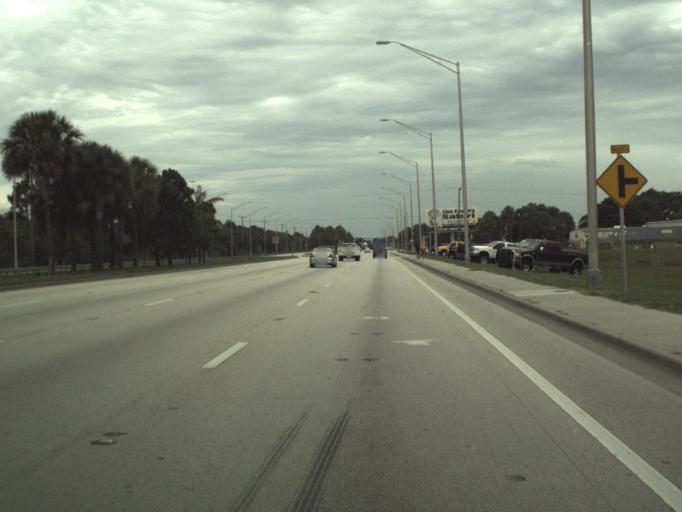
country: US
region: Florida
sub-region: Palm Beach County
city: Lake Belvedere Estates
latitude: 26.6798
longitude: -80.1770
